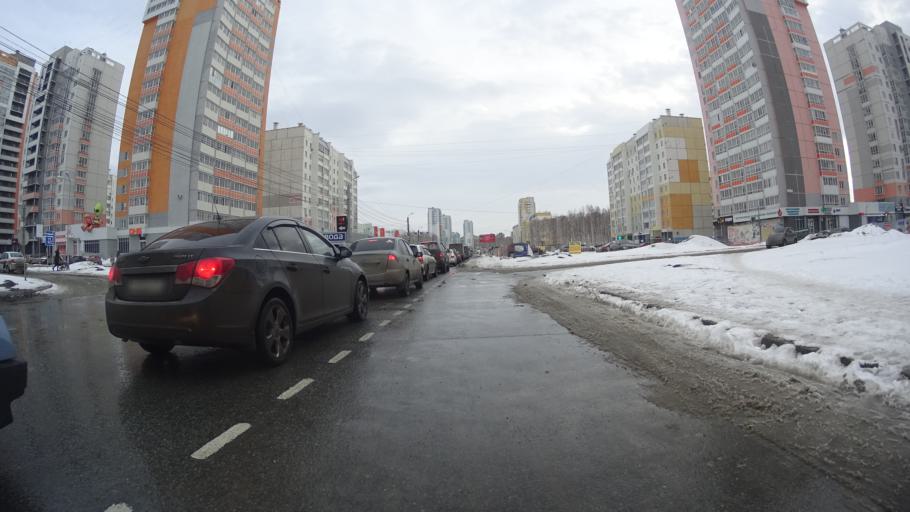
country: RU
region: Chelyabinsk
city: Roshchino
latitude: 55.2091
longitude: 61.2843
